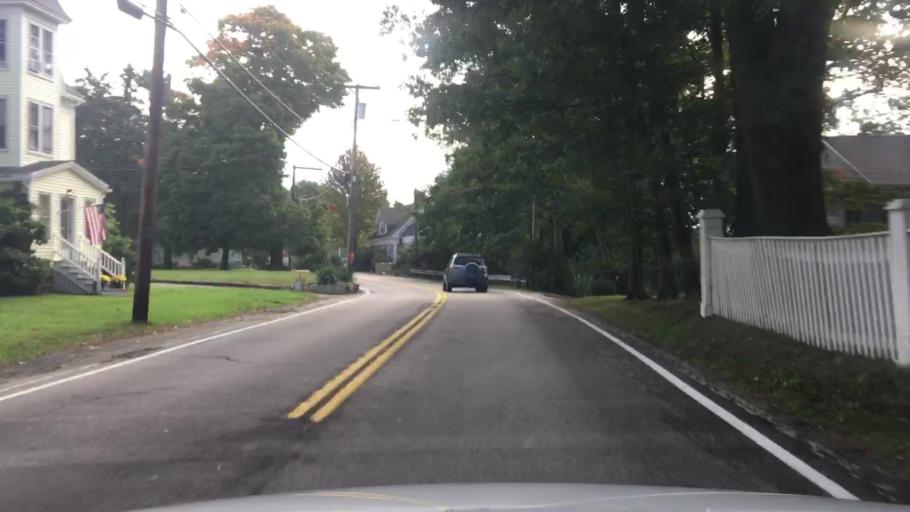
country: US
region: Maine
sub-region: York County
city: Kittery
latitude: 43.0856
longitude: -70.7297
